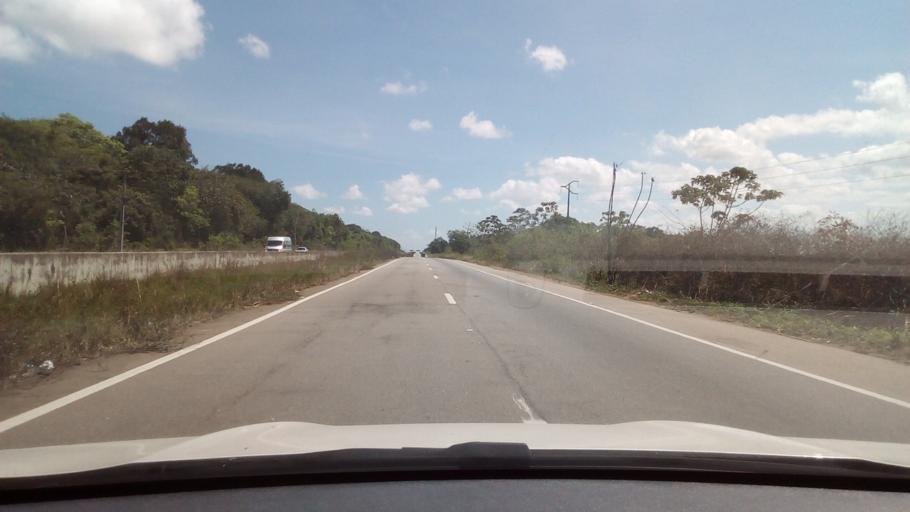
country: BR
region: Rio Grande do Norte
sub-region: Nisia Floresta
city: Nisia Floresta
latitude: -6.1296
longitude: -35.2287
